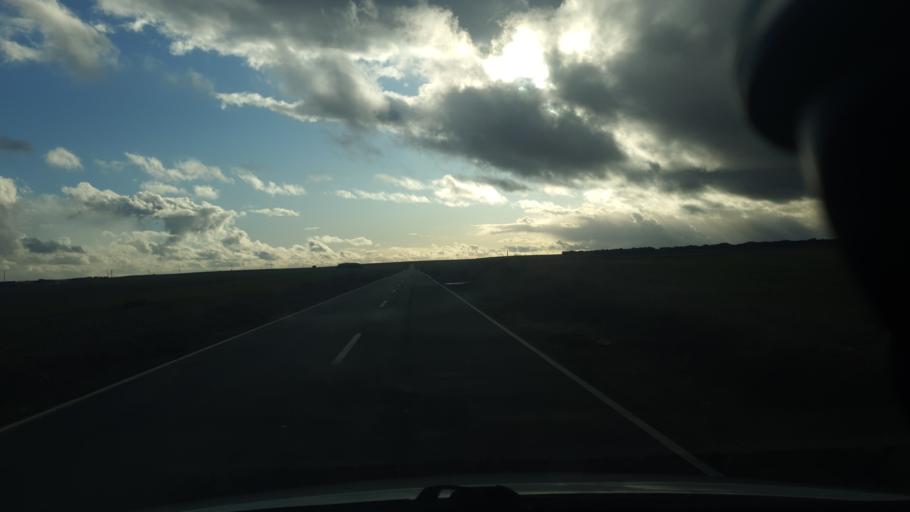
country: ES
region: Castille and Leon
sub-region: Provincia de Segovia
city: Santiuste de San Juan Bautista
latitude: 41.1397
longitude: -4.5916
